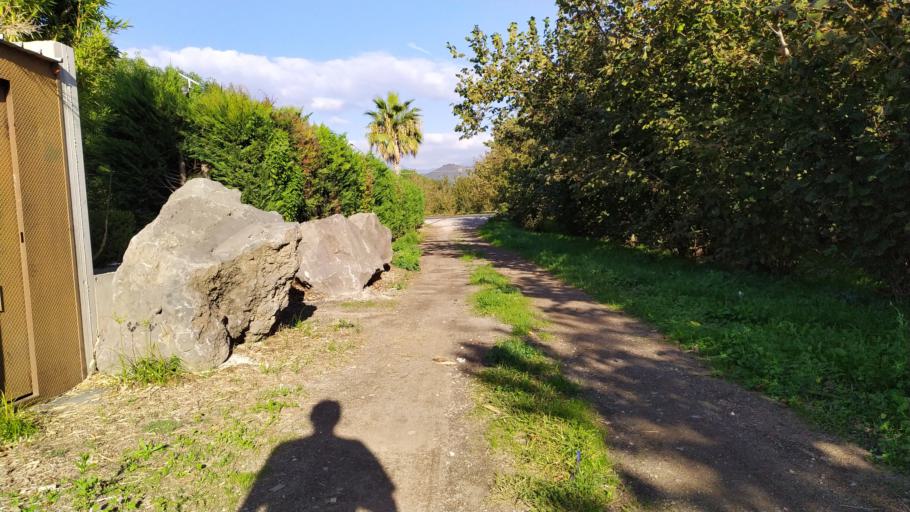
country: IT
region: Campania
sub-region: Provincia di Napoli
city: Piazzolla
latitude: 40.8916
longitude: 14.5310
